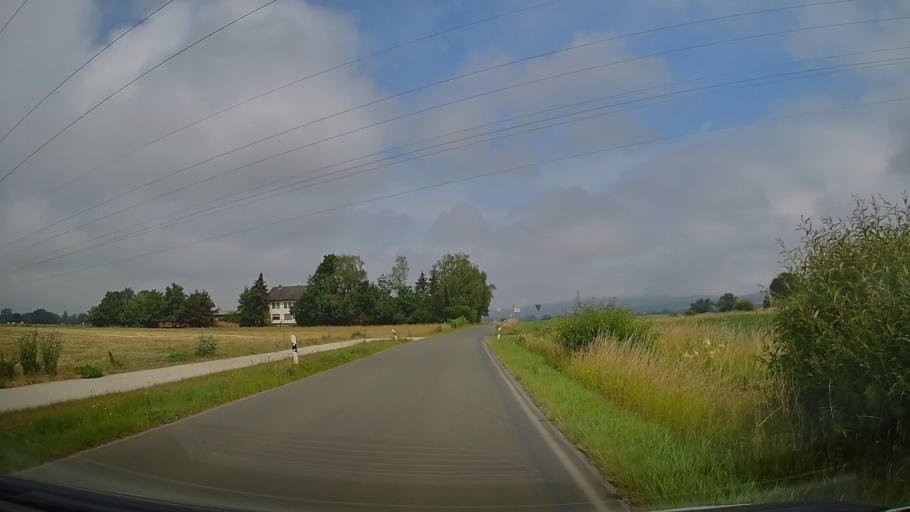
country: DE
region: Lower Saxony
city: Rinteln
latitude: 52.1728
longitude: 9.0310
